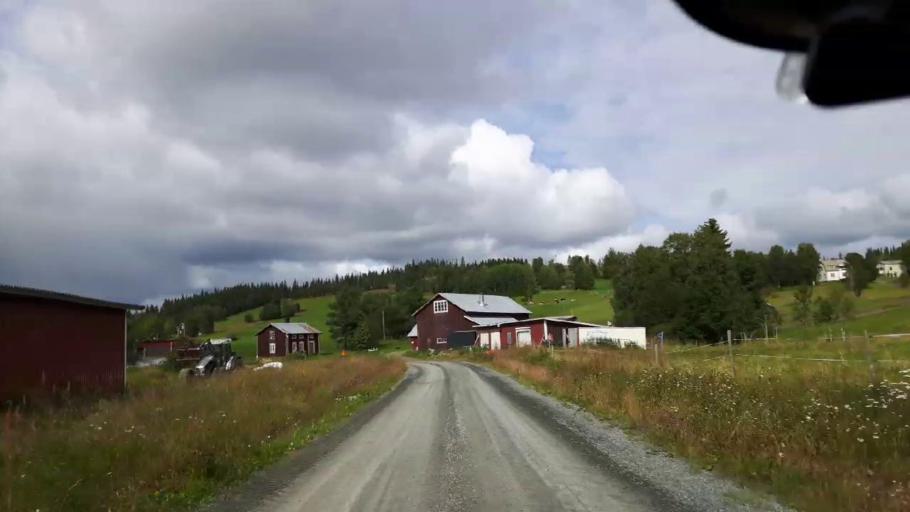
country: SE
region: Jaemtland
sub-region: Krokoms Kommun
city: Valla
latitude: 63.5769
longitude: 13.9042
